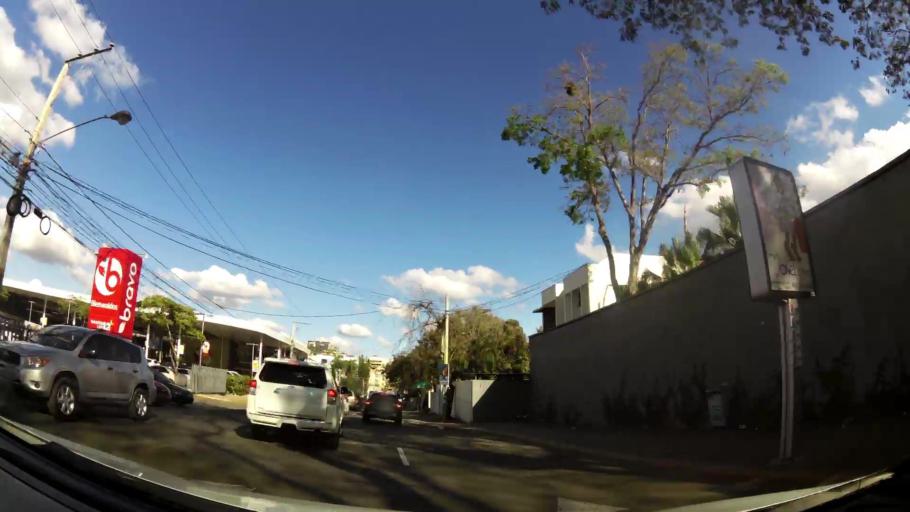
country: DO
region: Santiago
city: Santiago de los Caballeros
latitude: 19.4531
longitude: -70.6863
